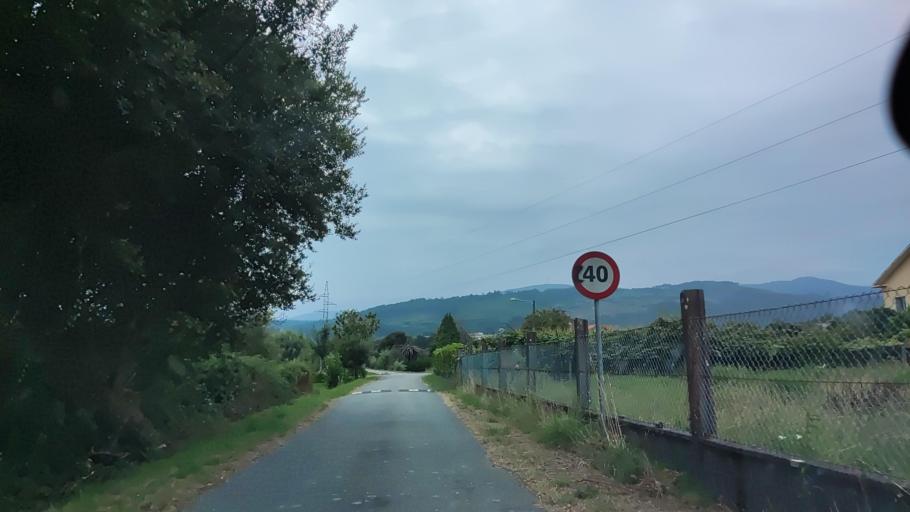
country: ES
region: Galicia
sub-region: Provincia da Coruna
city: Rois
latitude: 42.7144
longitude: -8.7048
